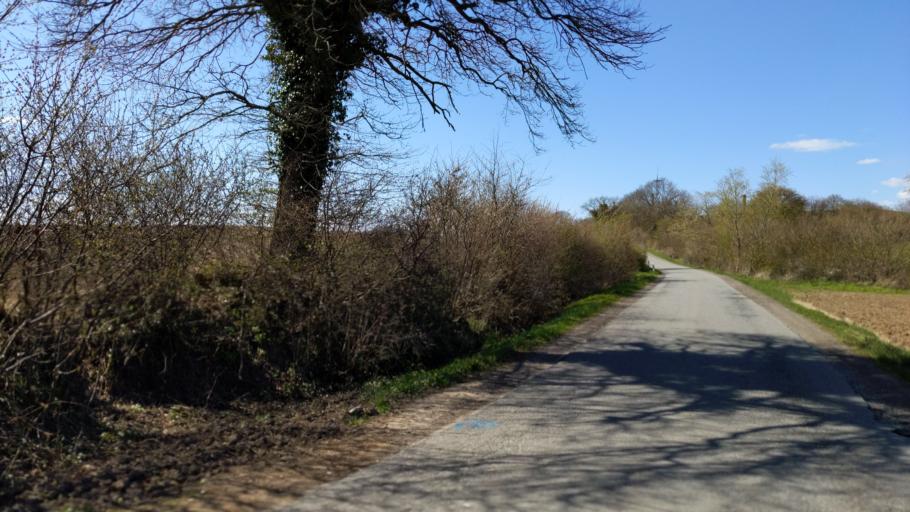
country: DE
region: Schleswig-Holstein
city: Sierksdorf
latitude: 54.1071
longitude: 10.7494
